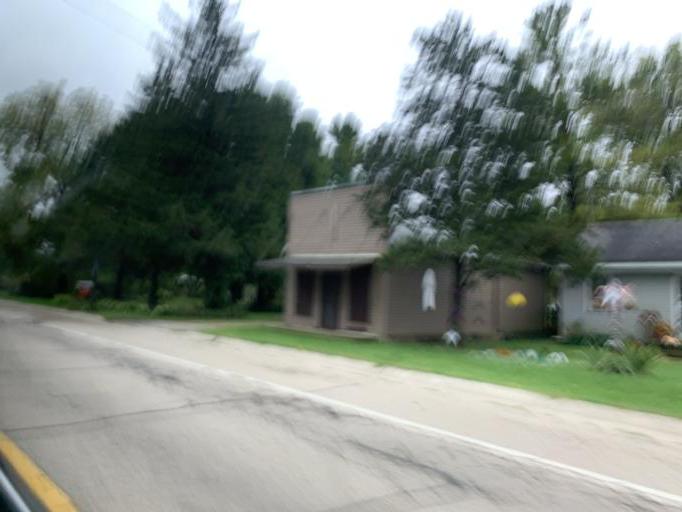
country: US
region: Wisconsin
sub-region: Grant County
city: Muscoda
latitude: 43.2198
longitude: -90.5497
